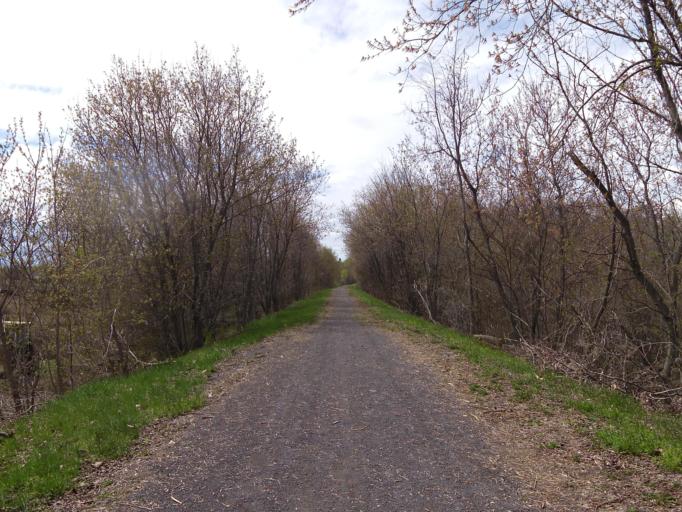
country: CA
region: Ontario
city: Hawkesbury
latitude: 45.5322
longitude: -74.6831
